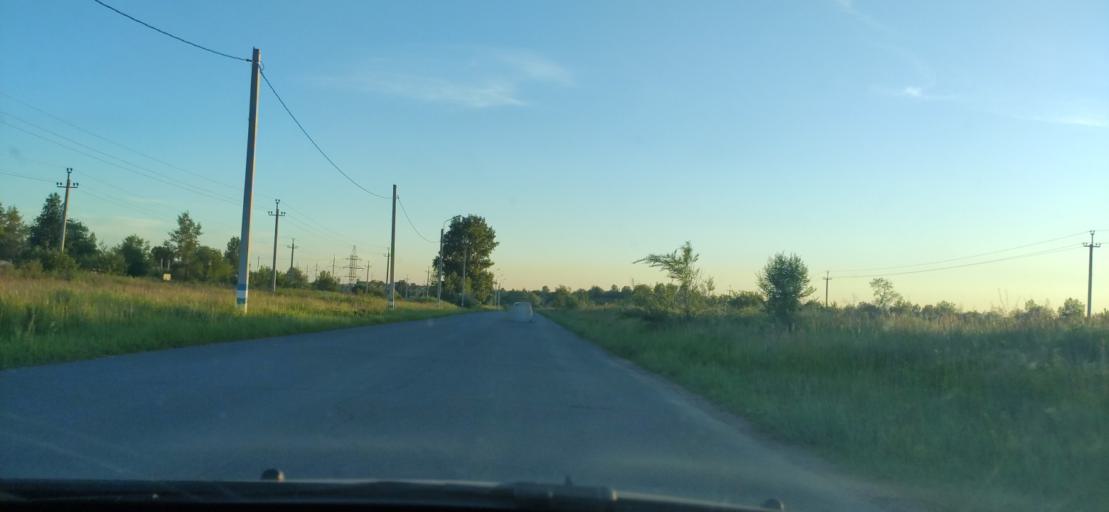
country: RU
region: Ulyanovsk
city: Mirnyy
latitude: 54.3771
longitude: 48.6612
